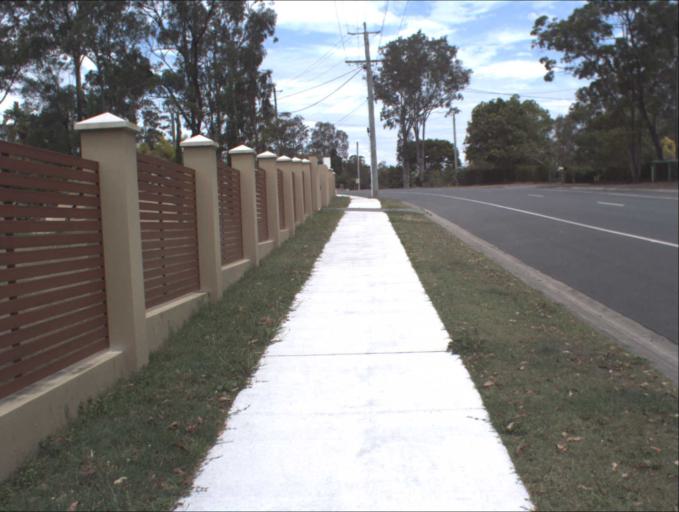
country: AU
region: Queensland
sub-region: Logan
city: Beenleigh
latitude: -27.6693
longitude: 153.2223
